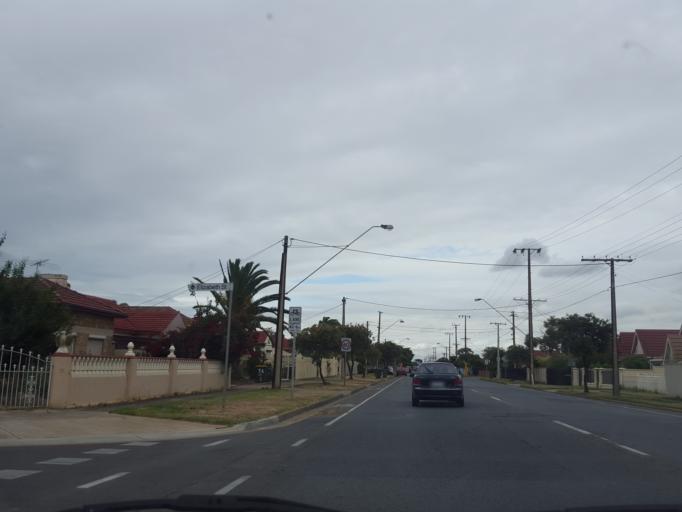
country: AU
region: South Australia
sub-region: Port Adelaide Enfield
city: Alberton
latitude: -34.8614
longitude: 138.5293
